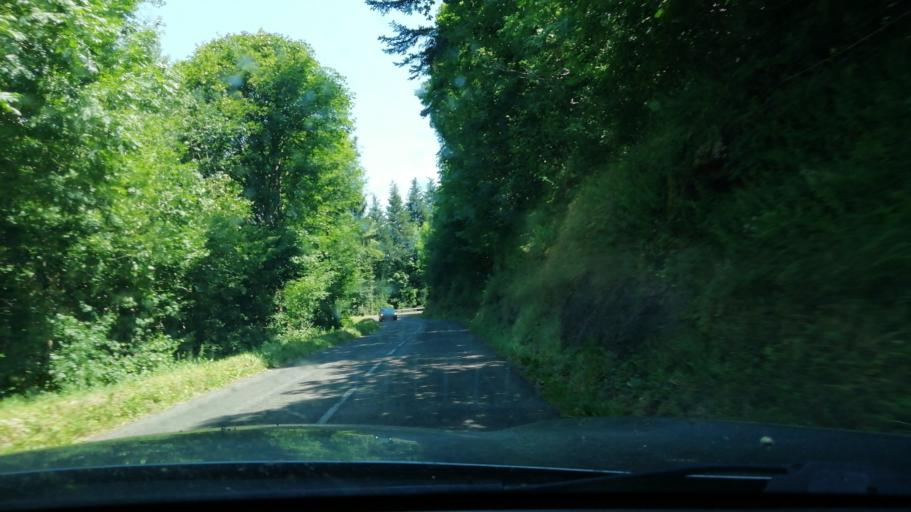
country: FR
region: Auvergne
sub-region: Departement du Cantal
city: Vic-sur-Cere
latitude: 45.0238
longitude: 2.5767
